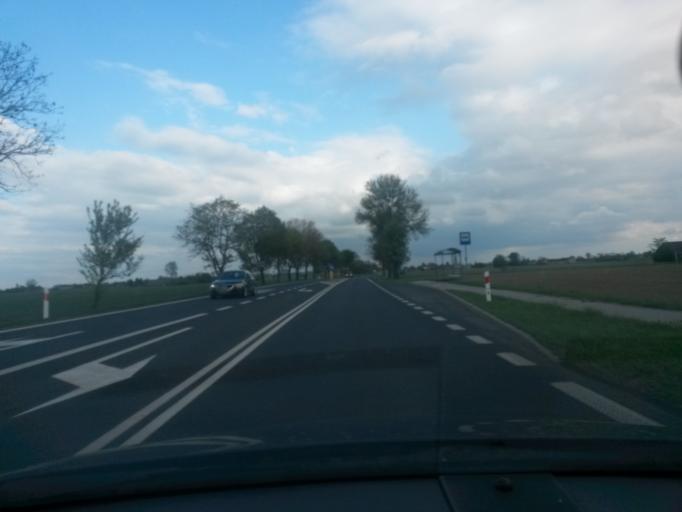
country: PL
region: Masovian Voivodeship
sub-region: Powiat plocki
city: Drobin
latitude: 52.7661
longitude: 19.9388
